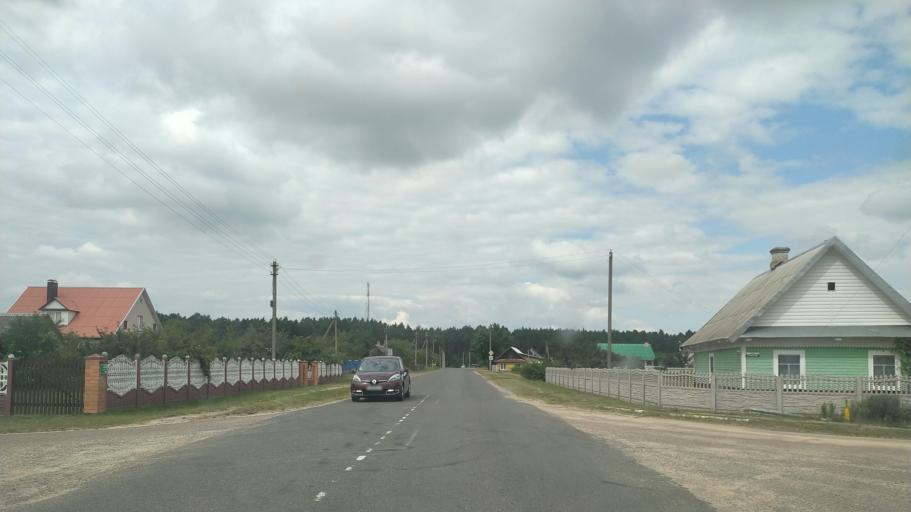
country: BY
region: Brest
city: Byaroza
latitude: 52.5445
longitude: 25.0676
